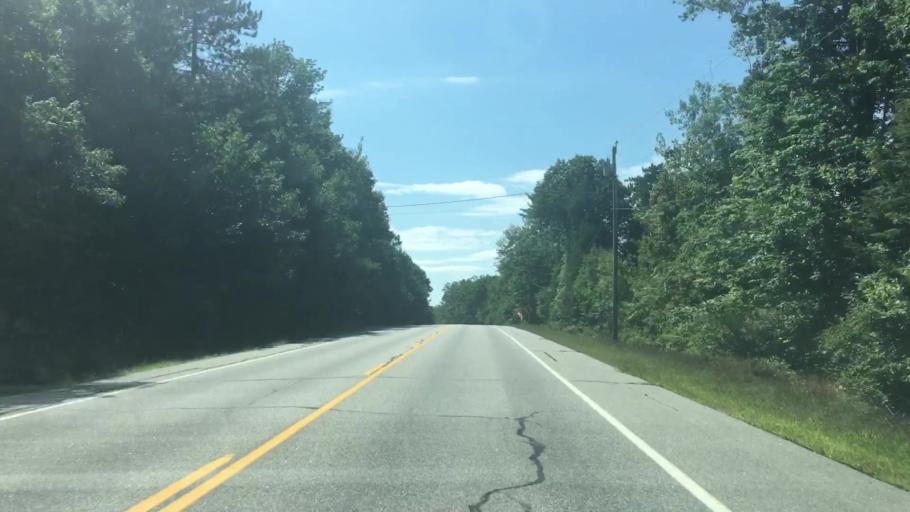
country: US
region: Maine
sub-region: Androscoggin County
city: Sabattus
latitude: 44.1370
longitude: -70.0582
